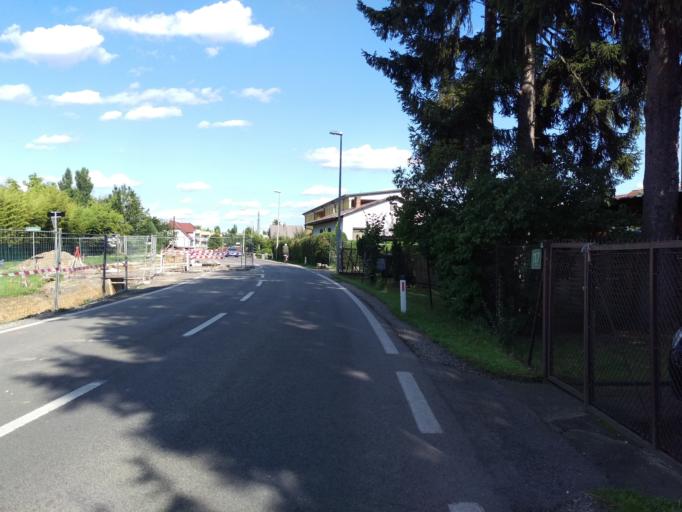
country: AT
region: Styria
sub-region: Graz Stadt
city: Wetzelsdorf
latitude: 47.0597
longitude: 15.3984
